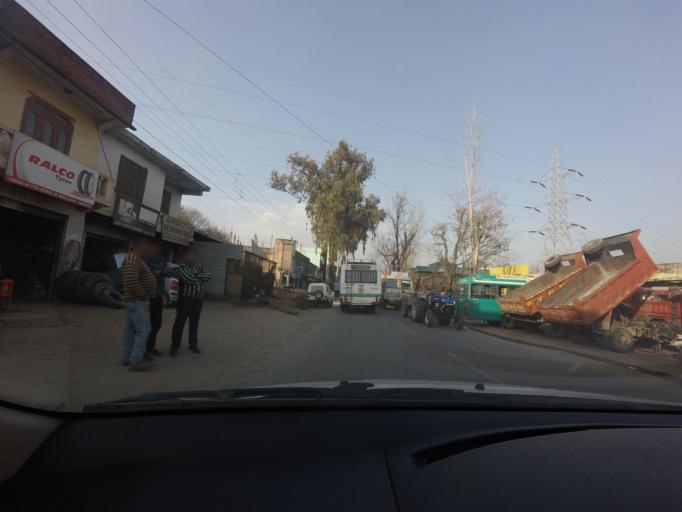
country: IN
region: Himachal Pradesh
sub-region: Mandi
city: Sundarnagar
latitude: 31.5570
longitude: 76.9018
